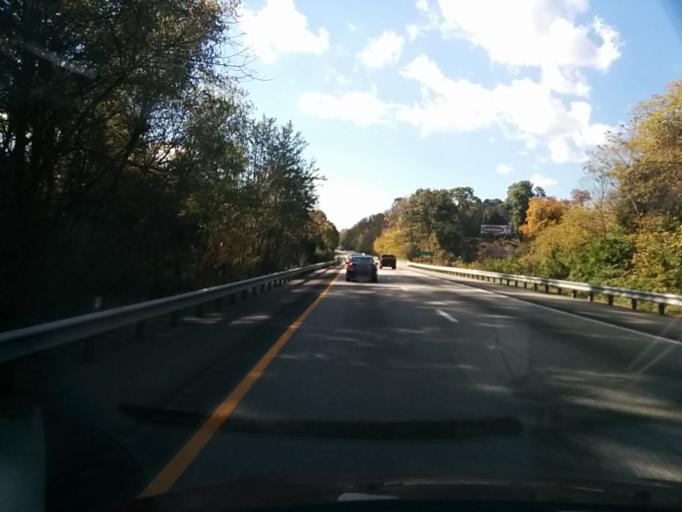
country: US
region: Virginia
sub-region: Botetourt County
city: Daleville
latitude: 37.4357
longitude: -79.8709
